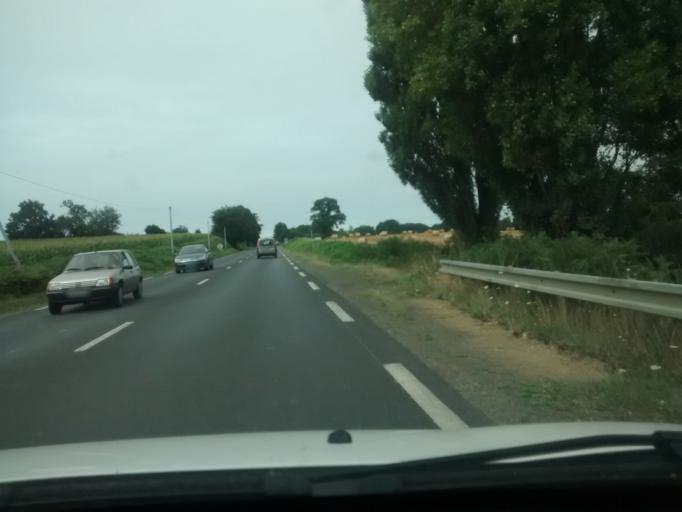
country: FR
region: Lower Normandy
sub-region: Departement de la Manche
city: Marcey-les-Greves
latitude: 48.7206
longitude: -1.4116
